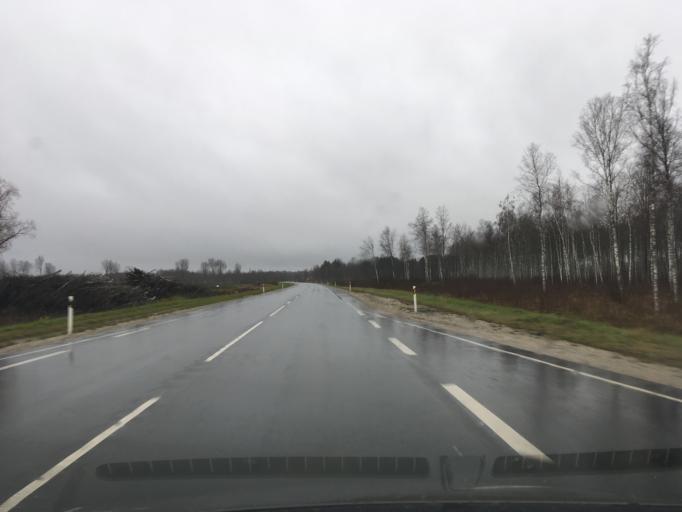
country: EE
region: Harju
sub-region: Nissi vald
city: Turba
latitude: 58.8573
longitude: 24.0719
